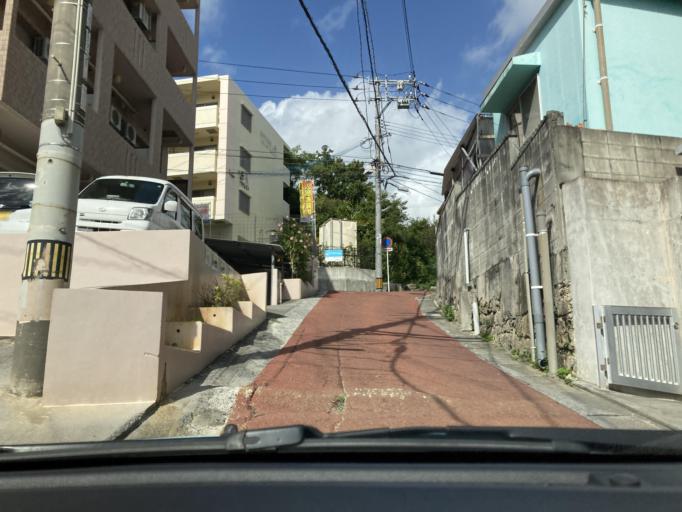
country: JP
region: Okinawa
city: Tomigusuku
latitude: 26.1967
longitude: 127.7004
